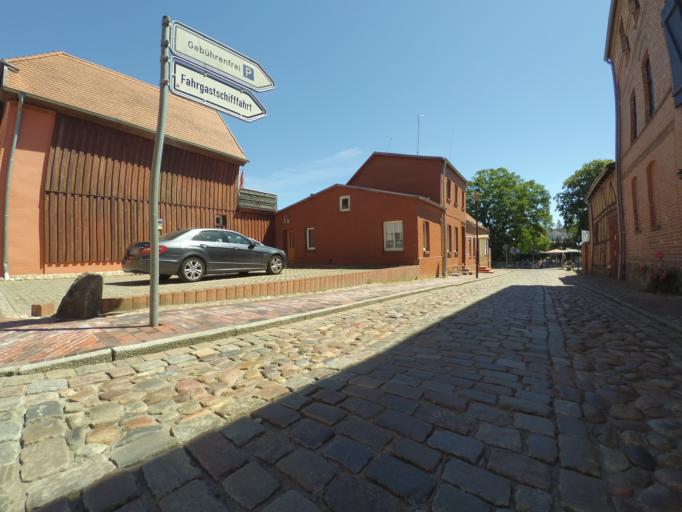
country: DE
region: Mecklenburg-Vorpommern
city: Plau am See
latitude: 53.4572
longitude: 12.2668
